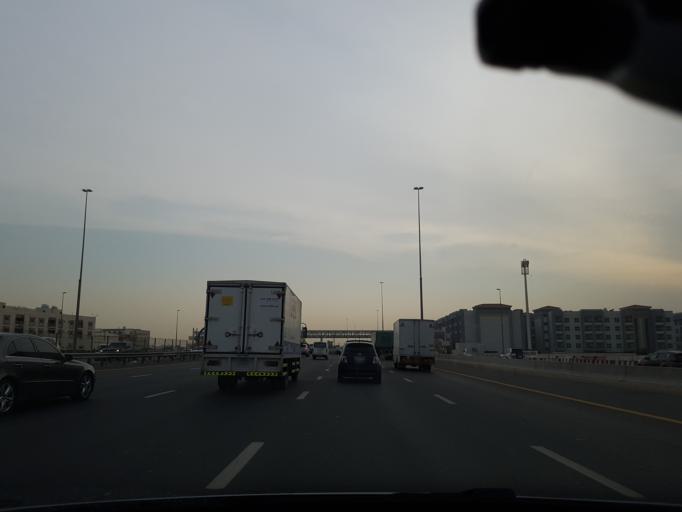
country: AE
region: Ash Shariqah
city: Sharjah
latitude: 25.2777
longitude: 55.4216
